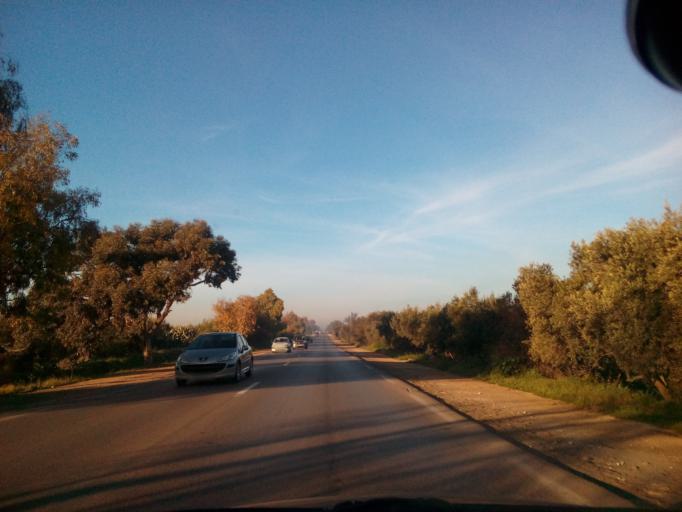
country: DZ
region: Relizane
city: Relizane
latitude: 35.7256
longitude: 0.3899
